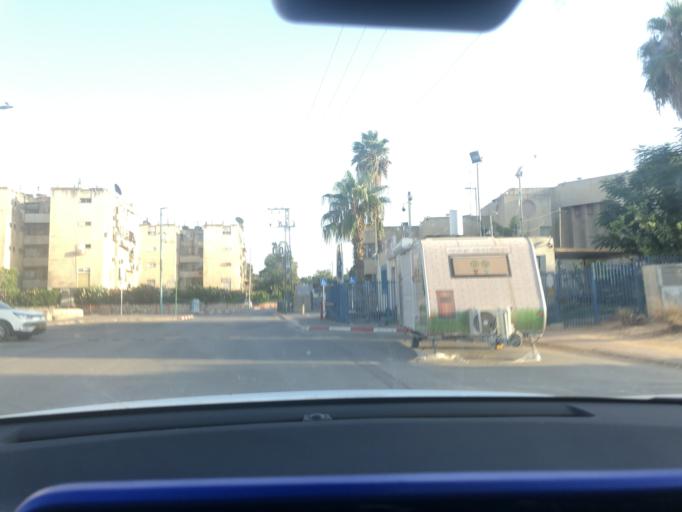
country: IL
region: Central District
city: Lod
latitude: 31.9542
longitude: 34.9013
